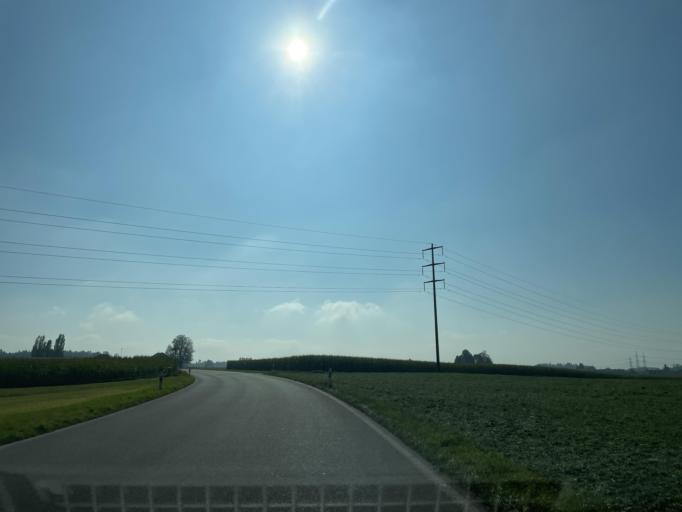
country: CH
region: Zurich
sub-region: Bezirk Winterthur
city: Brutten
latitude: 47.4671
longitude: 8.6675
